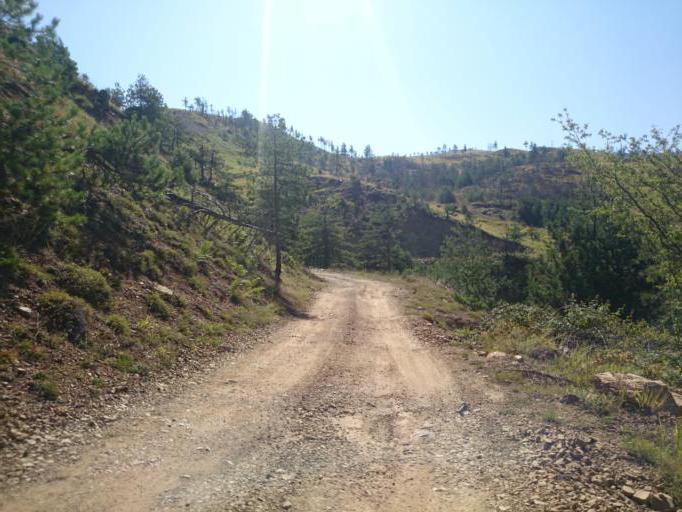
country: AL
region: Diber
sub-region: Rrethi i Bulqizes
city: Martanesh
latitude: 41.3925
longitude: 20.2611
